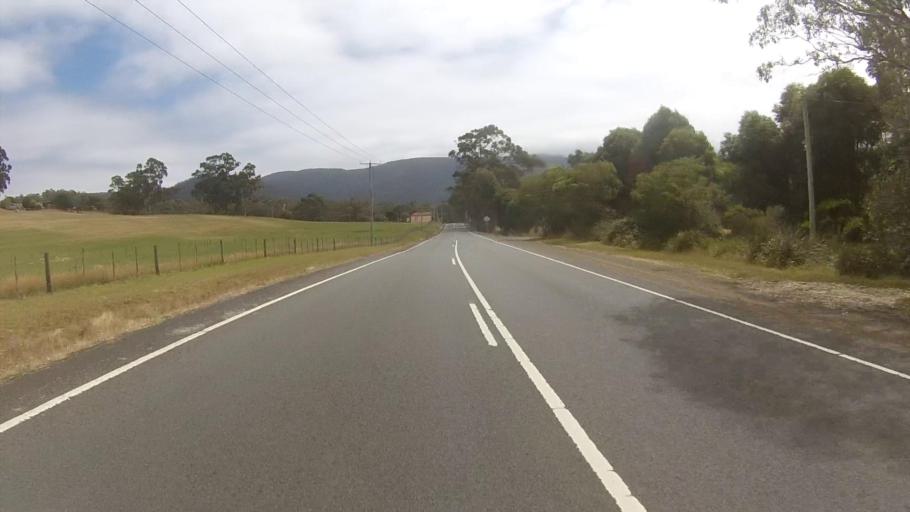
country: AU
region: Tasmania
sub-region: Kingborough
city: Margate
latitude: -42.9915
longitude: 147.1983
